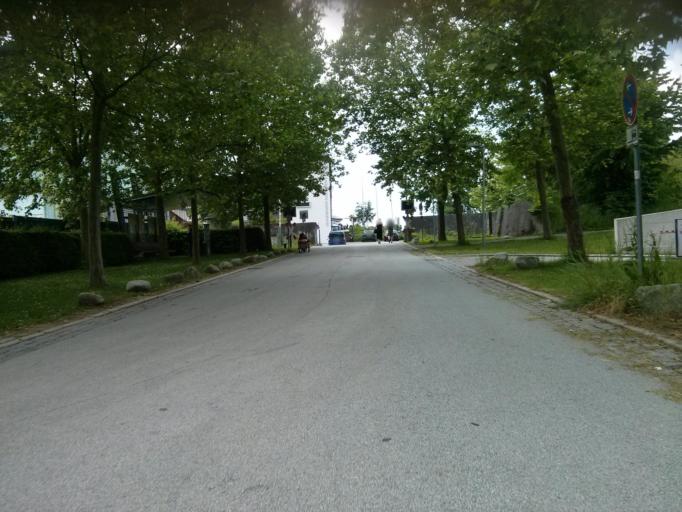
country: DE
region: Bavaria
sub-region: Lower Bavaria
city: Deggendorf
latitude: 48.8286
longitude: 12.9560
